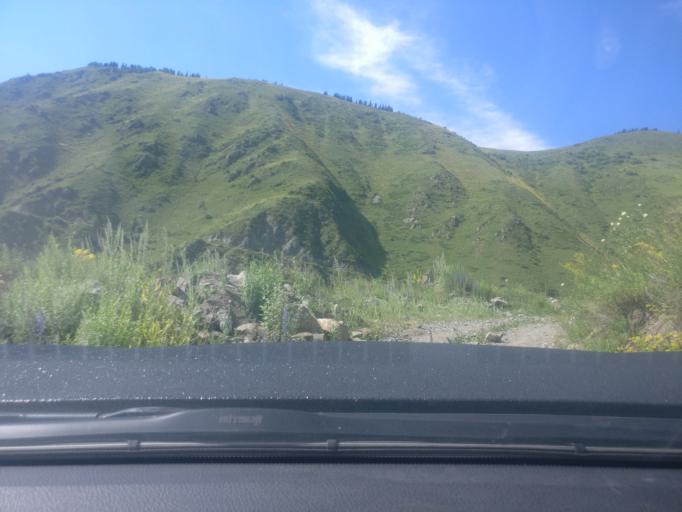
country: KZ
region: Almaty Qalasy
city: Almaty
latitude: 43.1032
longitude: 76.9504
